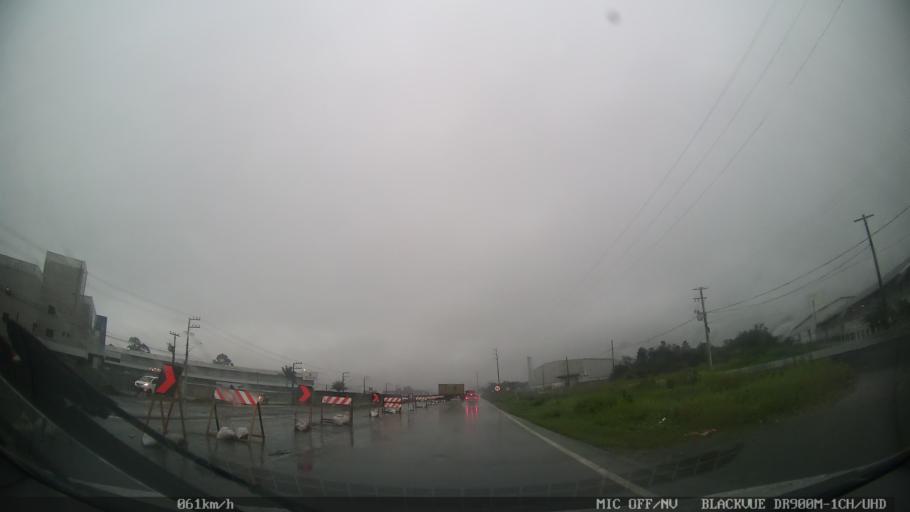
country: BR
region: Santa Catarina
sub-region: Navegantes
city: Navegantes
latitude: -26.8722
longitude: -48.6710
